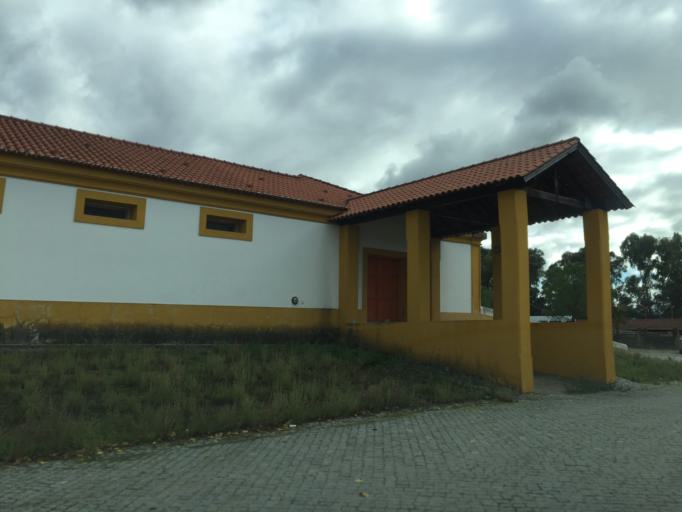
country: PT
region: Portalegre
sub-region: Alter do Chao
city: Alter do Chao
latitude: 39.2218
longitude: -7.6866
